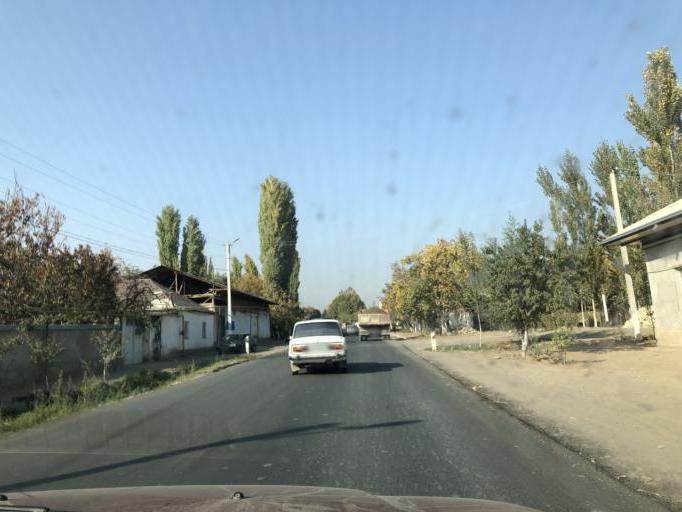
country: UZ
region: Namangan
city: Chust Shahri
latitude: 41.0702
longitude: 71.2046
